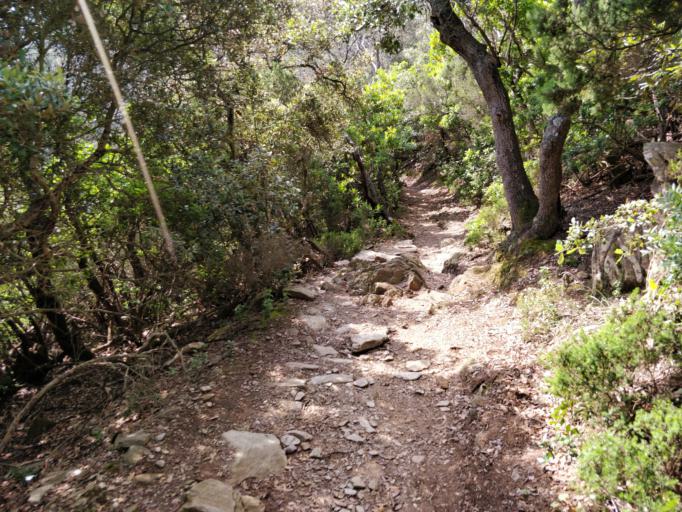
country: FR
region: Provence-Alpes-Cote d'Azur
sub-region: Departement du Var
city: Le Lavandou
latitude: 43.0117
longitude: 6.3895
